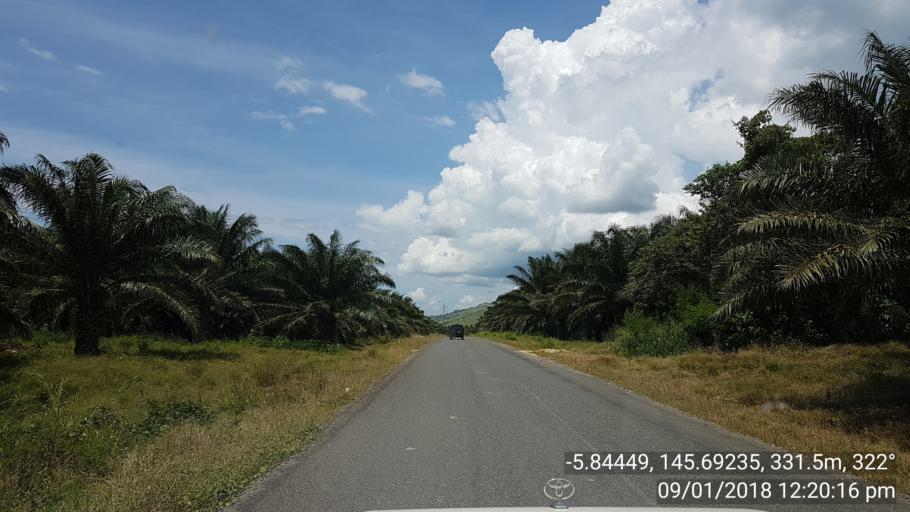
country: PG
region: Eastern Highlands
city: Goroka
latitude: -5.8450
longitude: 145.6926
